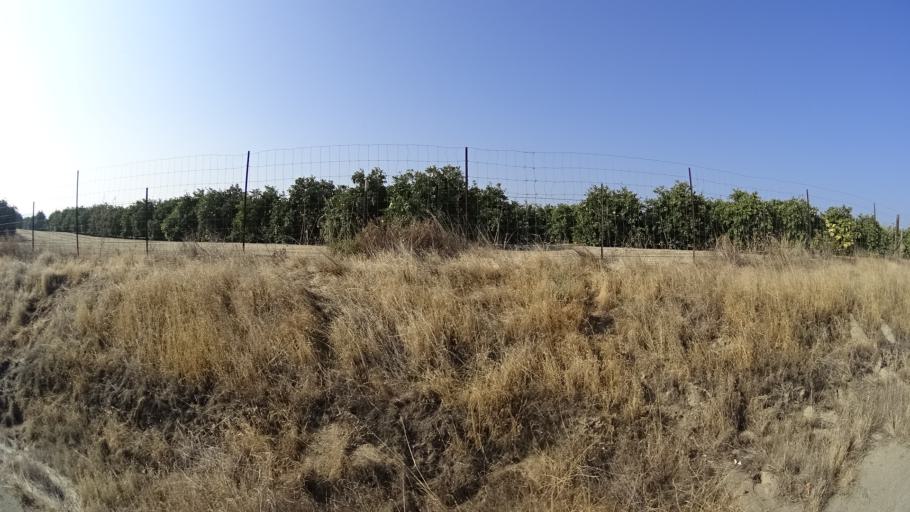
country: US
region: California
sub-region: Kern County
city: Oildale
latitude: 35.4355
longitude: -118.8280
